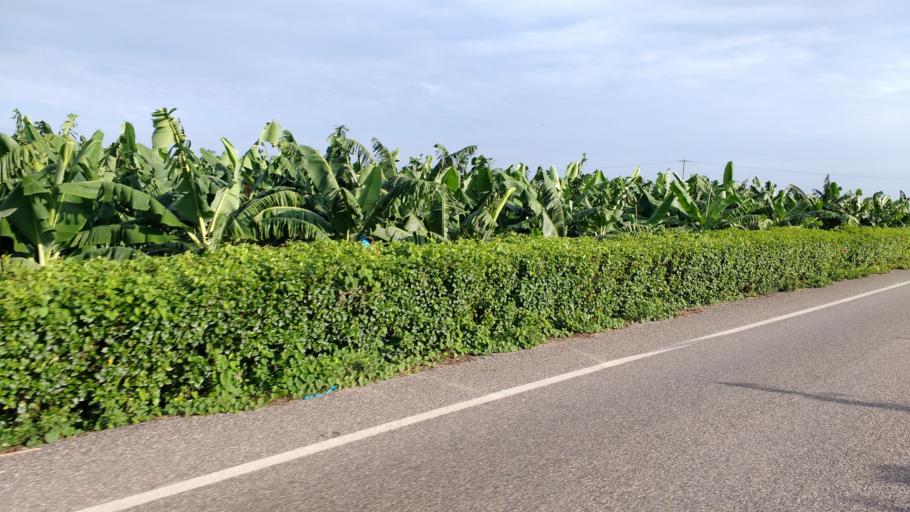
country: MX
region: Tabasco
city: Teapa
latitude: 17.6081
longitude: -92.9659
